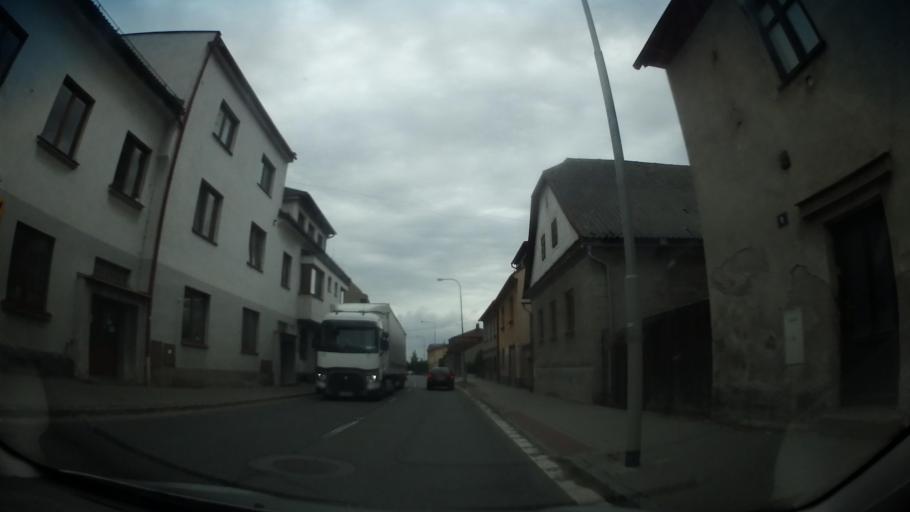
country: CZ
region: Vysocina
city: Krizova
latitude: 49.6890
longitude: 15.8501
